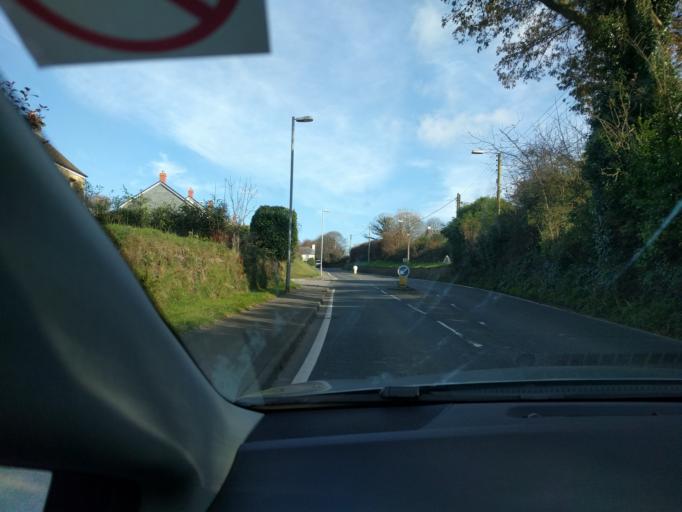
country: GB
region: England
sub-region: Cornwall
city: Camelford
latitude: 50.6244
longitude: -4.6728
